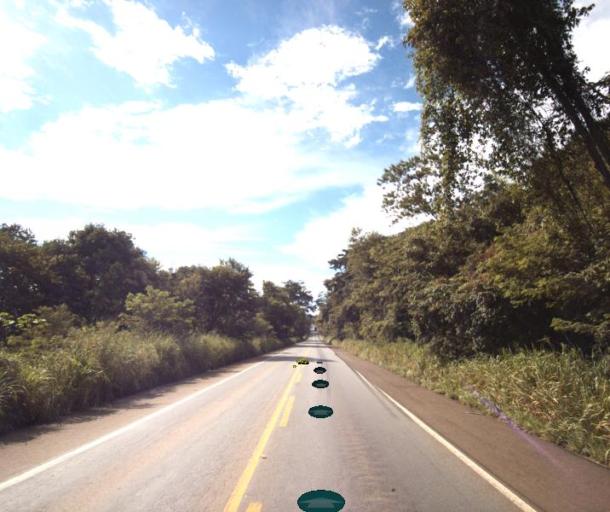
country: BR
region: Goias
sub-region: Jaragua
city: Jaragua
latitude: -15.6068
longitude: -49.4048
